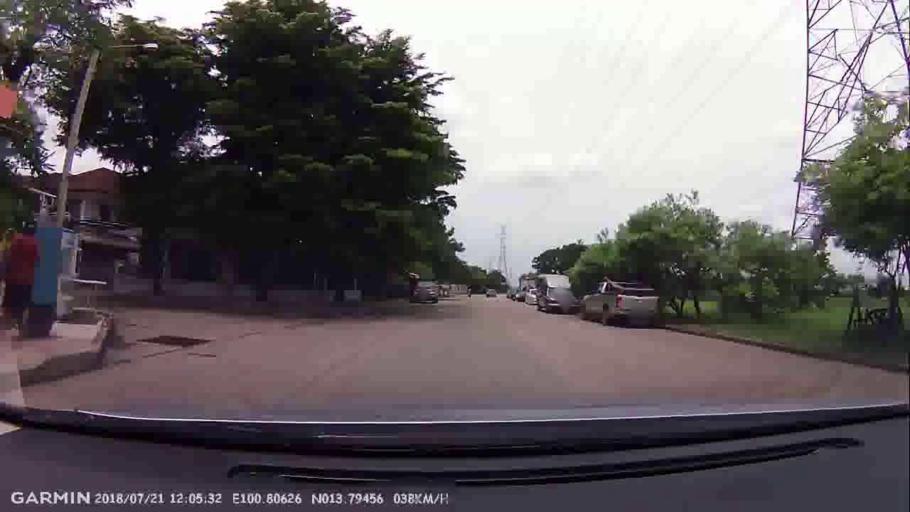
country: TH
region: Bangkok
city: Lat Krabang
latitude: 13.7944
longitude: 100.8064
